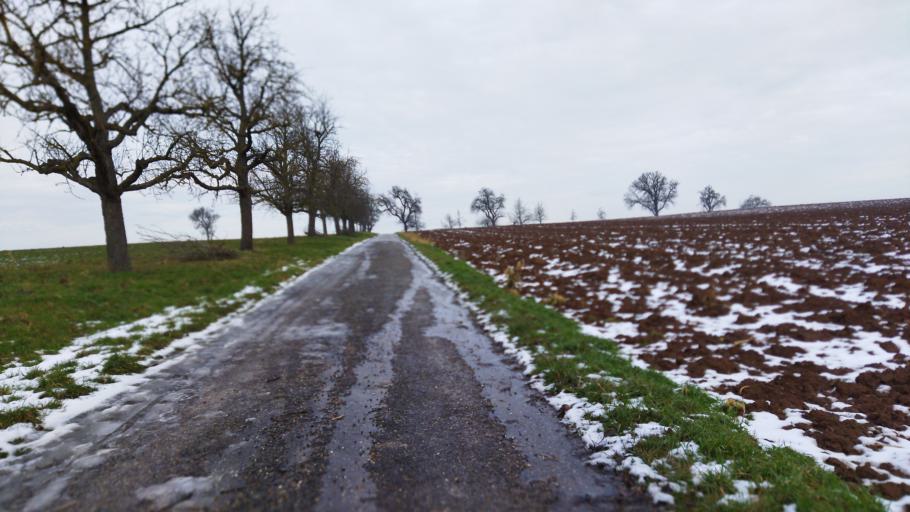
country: DE
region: Baden-Wuerttemberg
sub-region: Regierungsbezirk Stuttgart
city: Untereisesheim
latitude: 49.1887
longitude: 9.1913
